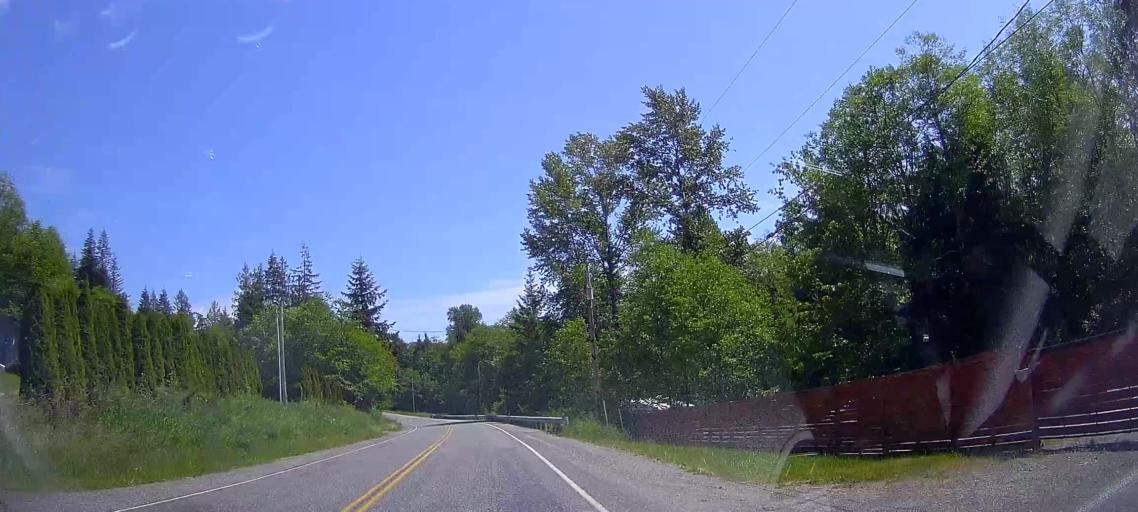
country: US
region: Washington
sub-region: Skagit County
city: Big Lake
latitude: 48.3929
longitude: -122.2659
